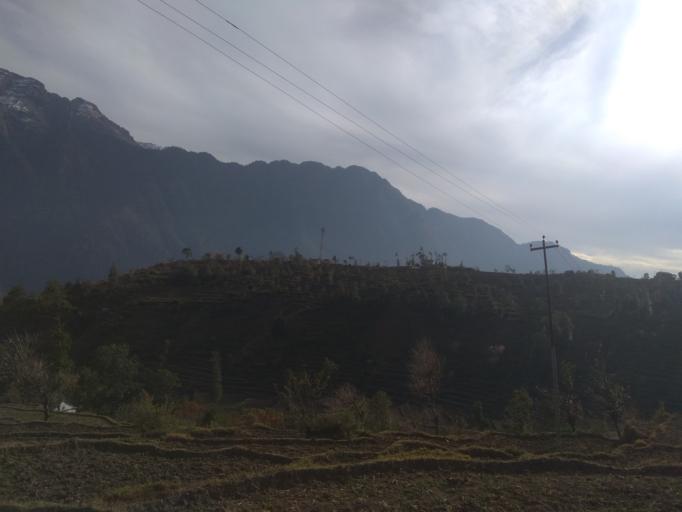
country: NP
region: Mid Western
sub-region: Bheri Zone
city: Dailekh
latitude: 29.2516
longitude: 81.6642
